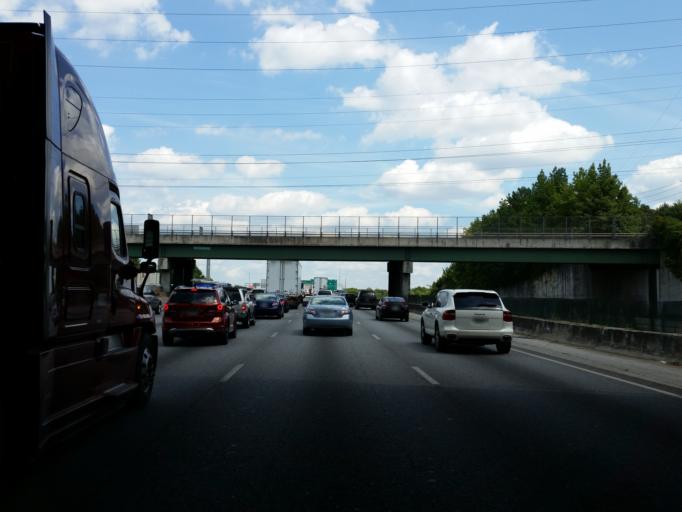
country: US
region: Georgia
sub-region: DeKalb County
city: Doraville
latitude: 33.9048
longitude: -84.2777
